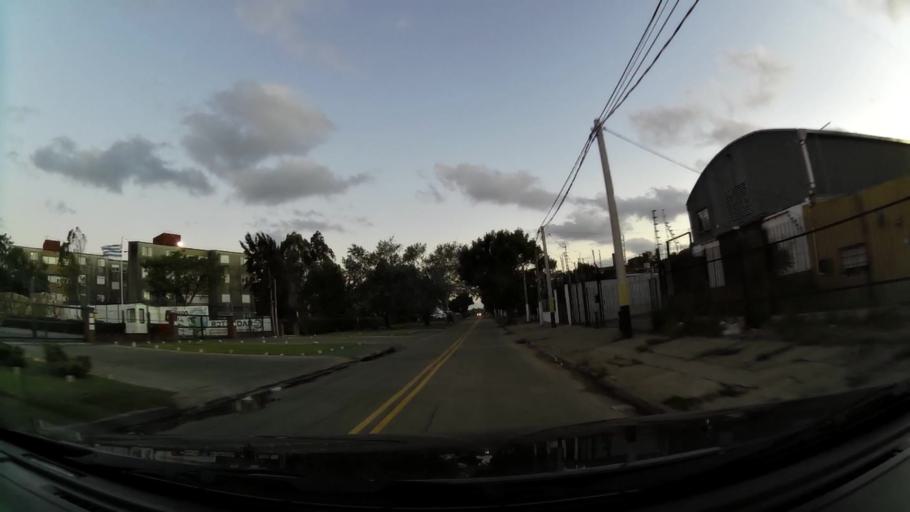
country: UY
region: Canelones
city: Paso de Carrasco
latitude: -34.8736
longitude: -56.1048
